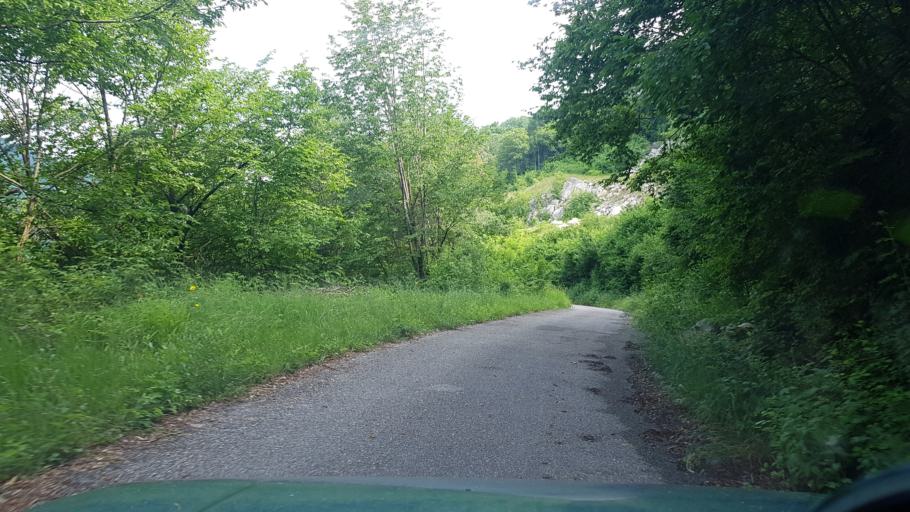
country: IT
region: Friuli Venezia Giulia
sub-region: Provincia di Udine
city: Torreano
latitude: 46.1648
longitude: 13.4409
